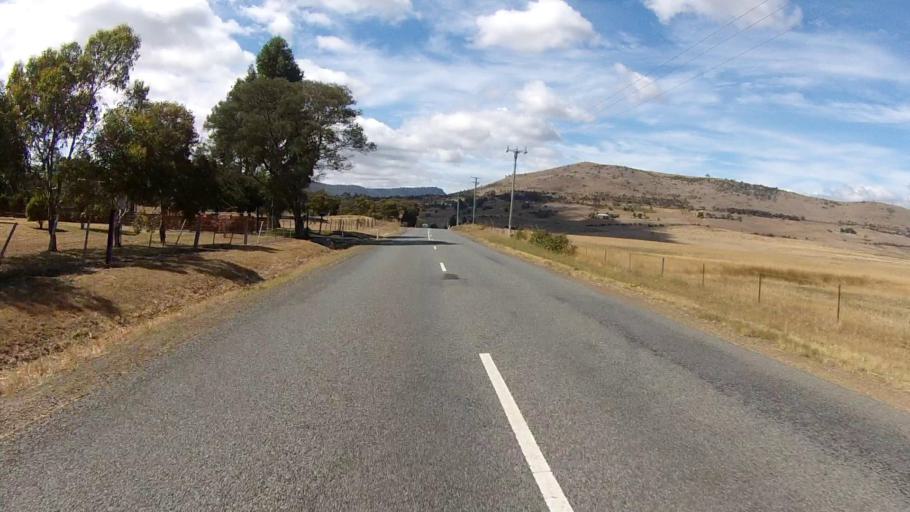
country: AU
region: Tasmania
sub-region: Brighton
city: Bridgewater
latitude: -42.7173
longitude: 147.2766
